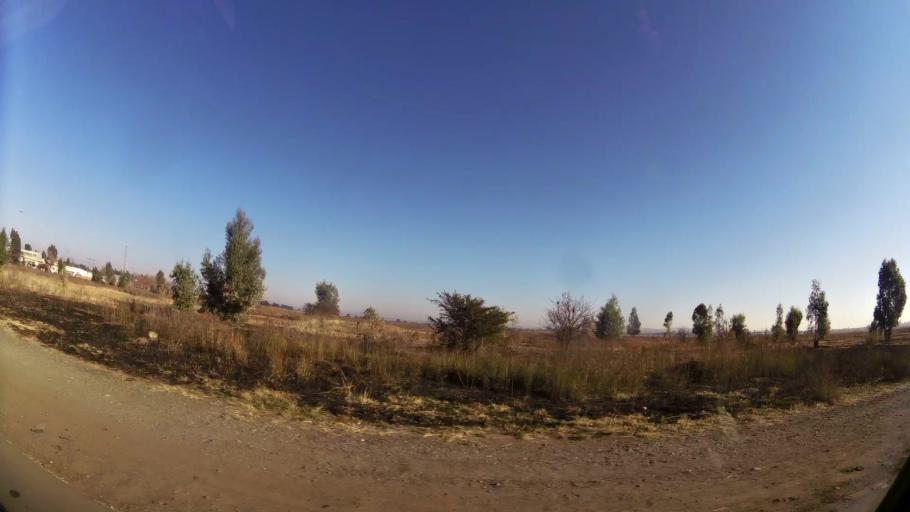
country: ZA
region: Gauteng
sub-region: Ekurhuleni Metropolitan Municipality
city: Germiston
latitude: -26.3427
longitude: 28.1308
